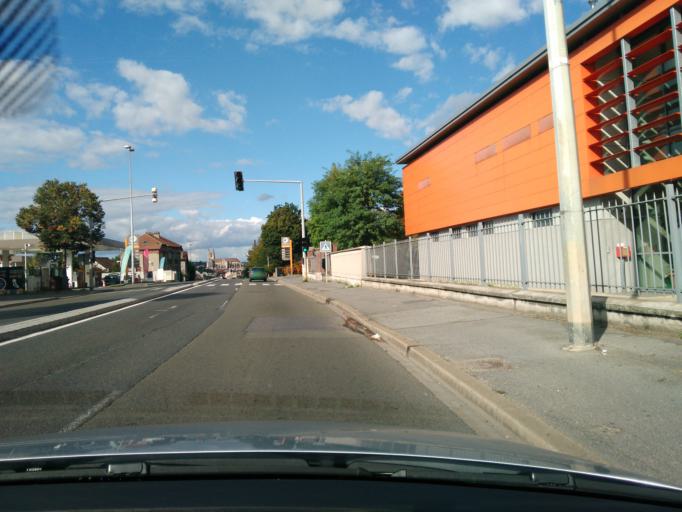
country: FR
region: Ile-de-France
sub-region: Departement de Seine-et-Marne
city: Meaux
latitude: 48.9483
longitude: 2.8801
